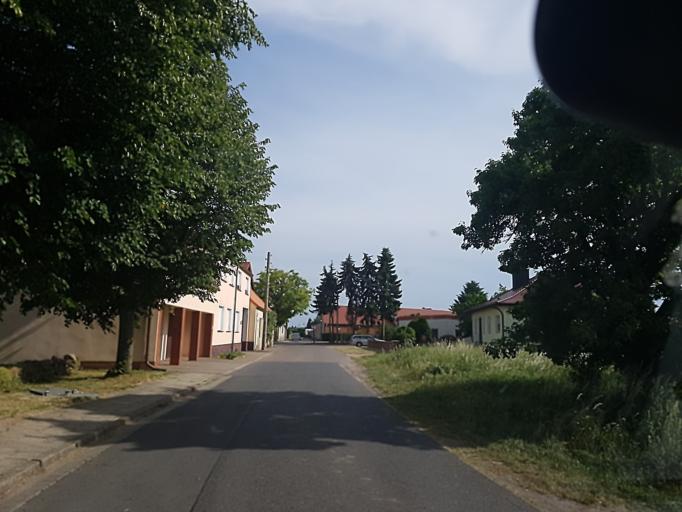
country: DE
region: Saxony-Anhalt
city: Kropstadt
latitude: 51.9901
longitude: 12.6786
